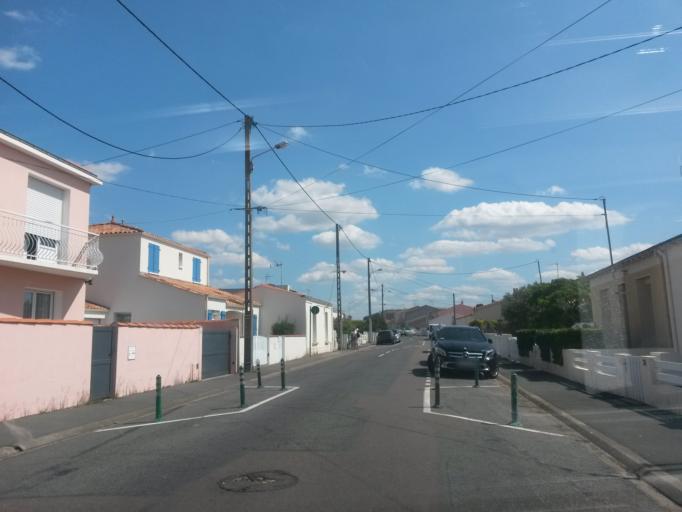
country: FR
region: Pays de la Loire
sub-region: Departement de la Vendee
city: Les Sables-d'Olonne
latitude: 46.4967
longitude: -1.8045
